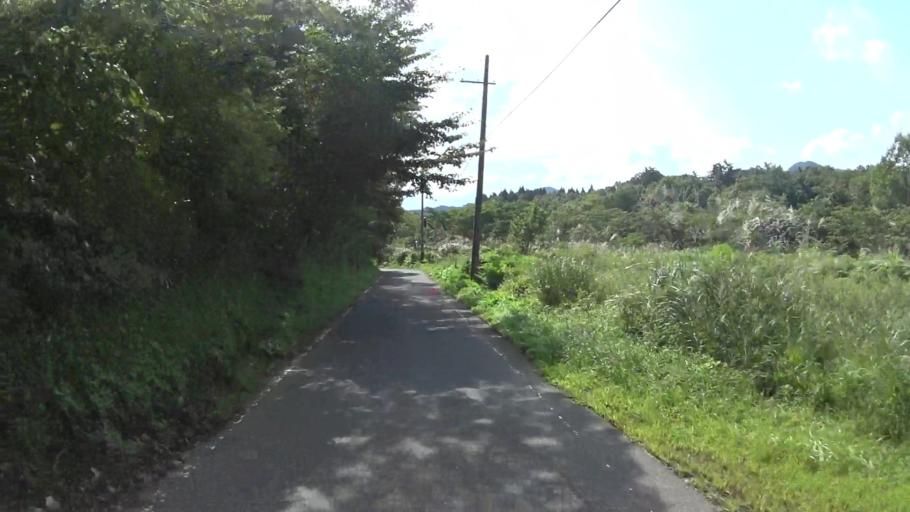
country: JP
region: Kyoto
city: Miyazu
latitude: 35.6461
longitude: 135.1809
